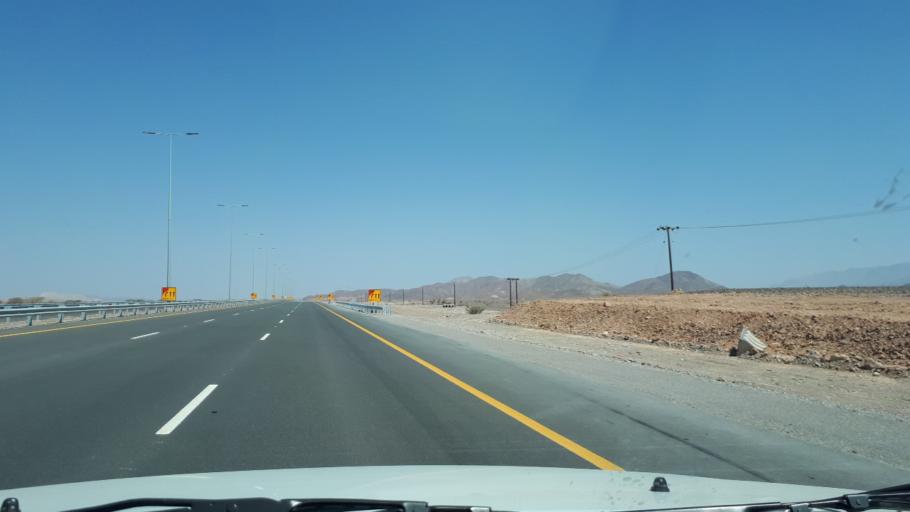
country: OM
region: Ash Sharqiyah
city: Badiyah
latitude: 22.4644
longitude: 58.9998
